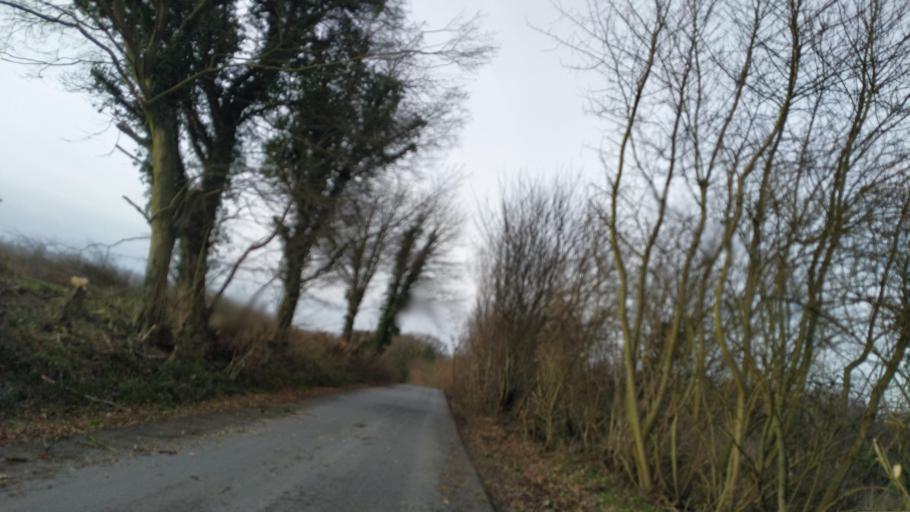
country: DE
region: Schleswig-Holstein
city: Malente
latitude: 54.1973
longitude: 10.6026
